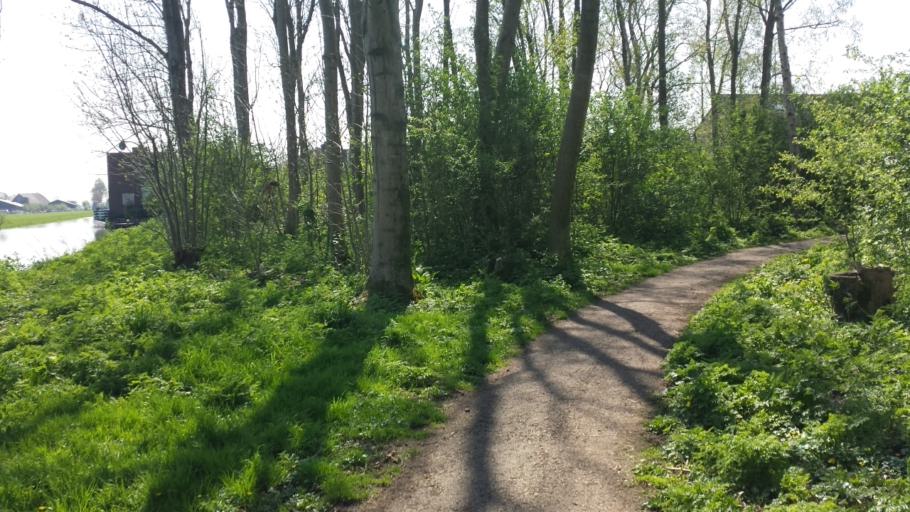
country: NL
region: South Holland
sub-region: Gemeente Vlist
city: Haastrecht
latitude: 51.9769
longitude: 4.7734
